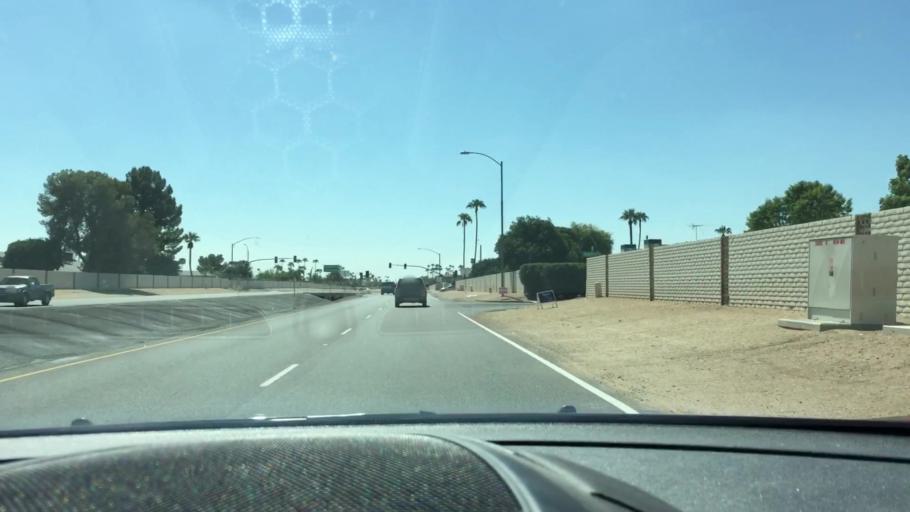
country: US
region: Arizona
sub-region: Maricopa County
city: Sun City
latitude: 33.6481
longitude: -112.2775
